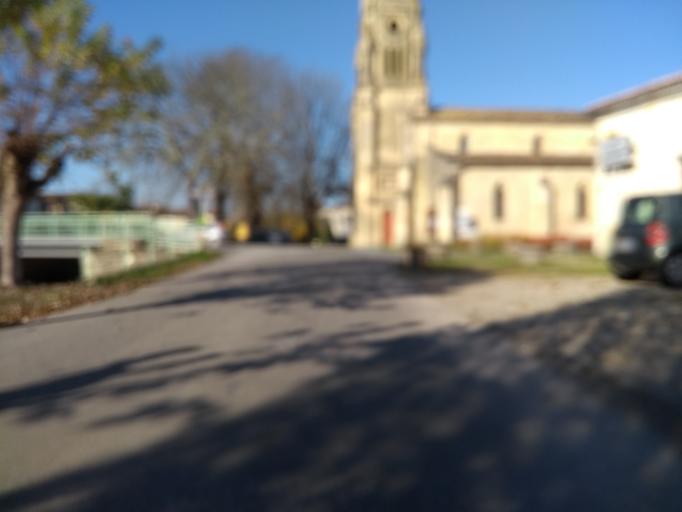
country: FR
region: Aquitaine
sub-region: Departement de la Gironde
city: Cambes
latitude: 44.7245
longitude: -0.4723
